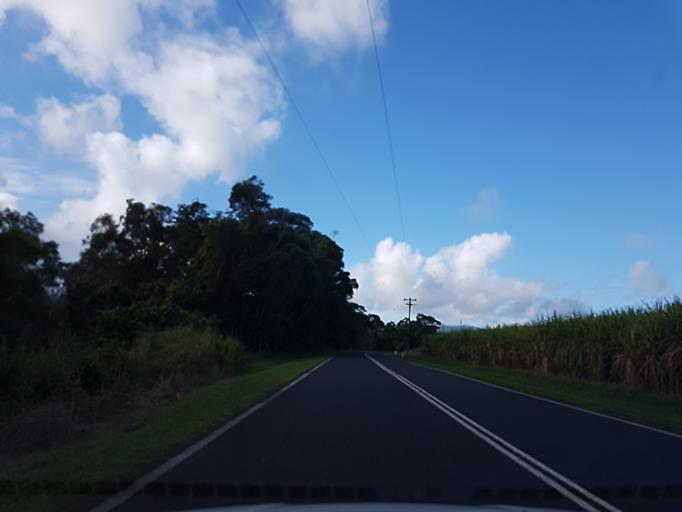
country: AU
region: Queensland
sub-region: Cairns
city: Port Douglas
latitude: -16.2786
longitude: 145.3828
